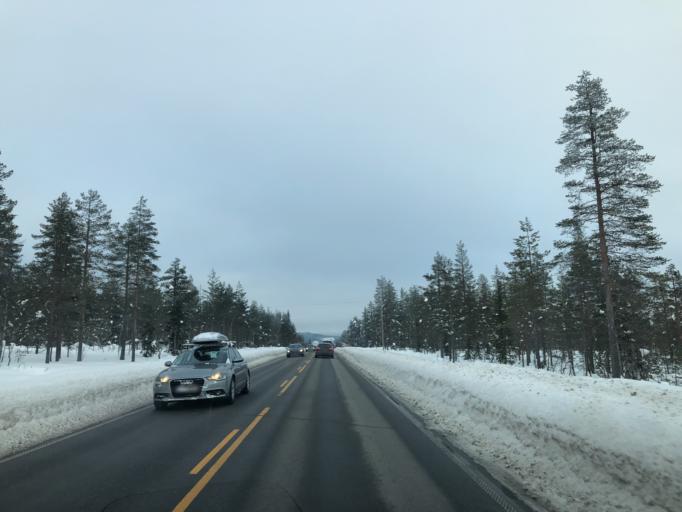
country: NO
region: Hedmark
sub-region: Trysil
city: Innbygda
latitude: 61.2405
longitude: 12.2748
